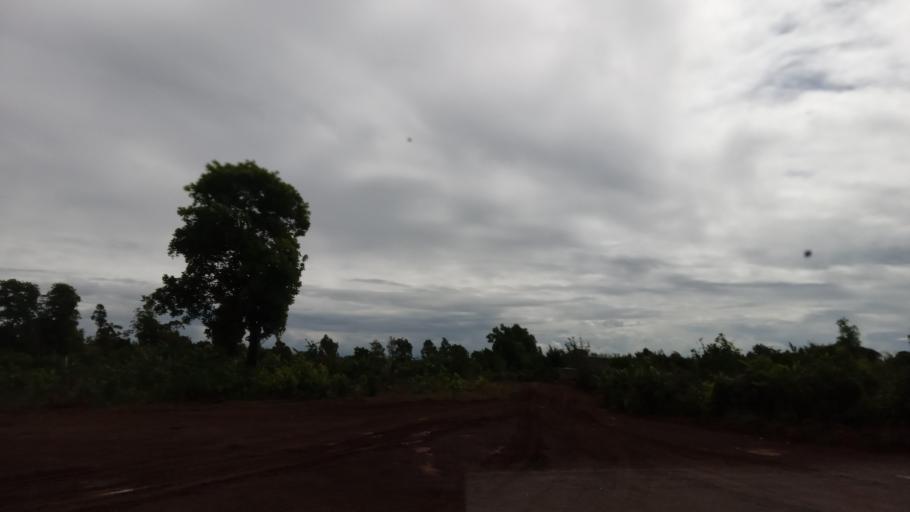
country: MG
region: Atsimo-Atsinanana
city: Vohipaho
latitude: -23.7808
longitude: 47.5463
